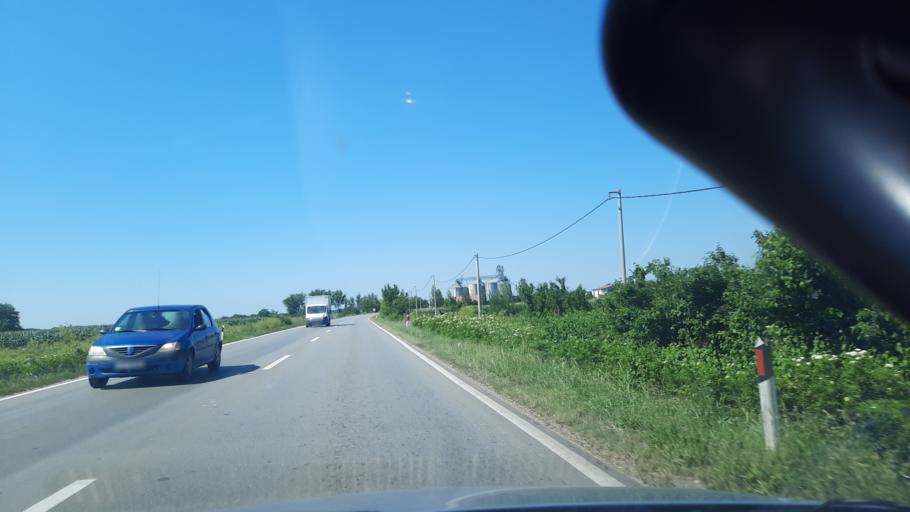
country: RS
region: Central Serbia
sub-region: Branicevski Okrug
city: Pozarevac
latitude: 44.6246
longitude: 21.1451
